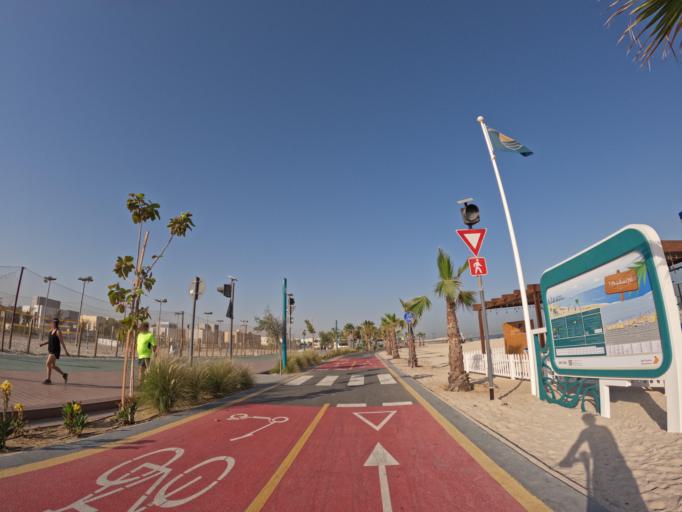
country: AE
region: Dubai
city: Dubai
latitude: 25.1657
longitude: 55.2088
